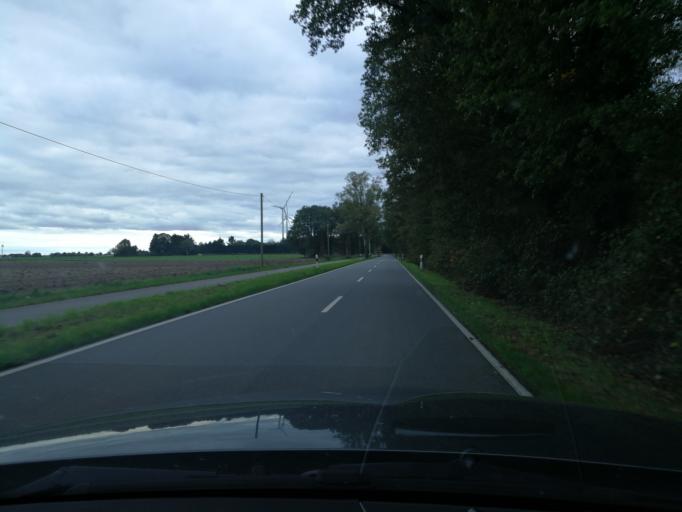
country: NL
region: Limburg
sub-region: Gemeente Venlo
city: Arcen
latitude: 51.4780
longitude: 6.2223
